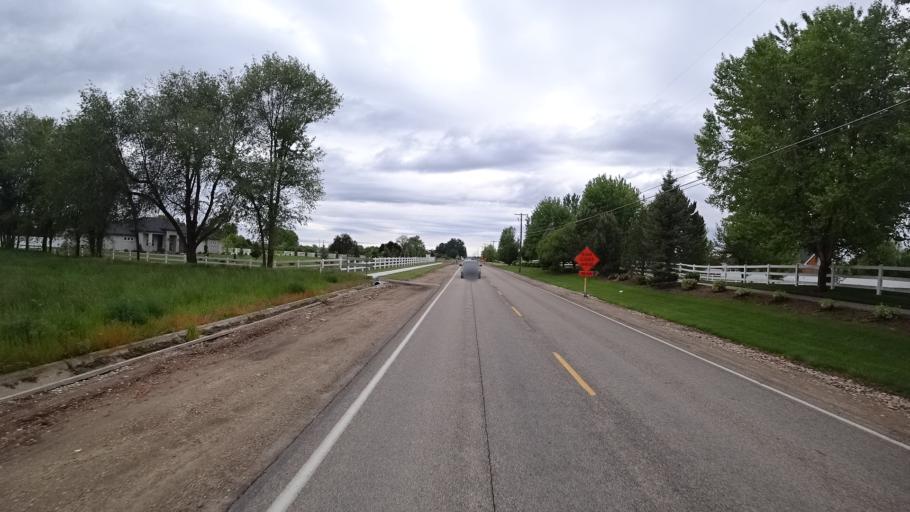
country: US
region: Idaho
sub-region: Ada County
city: Eagle
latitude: 43.7062
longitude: -116.3996
